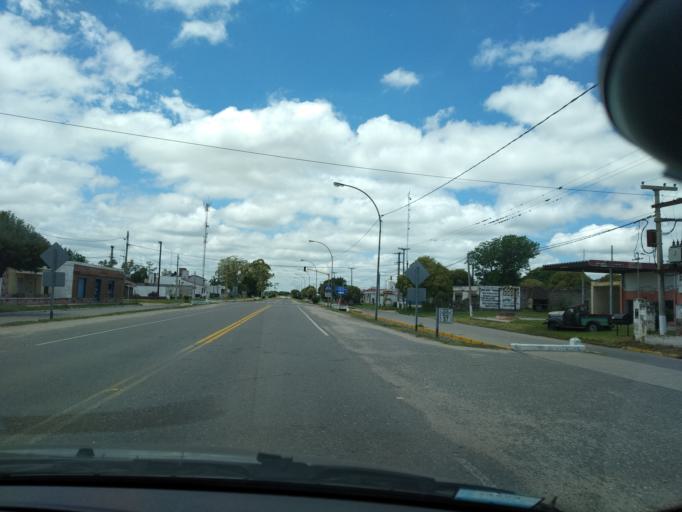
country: AR
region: Cordoba
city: Toledo
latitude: -31.6497
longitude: -64.0880
